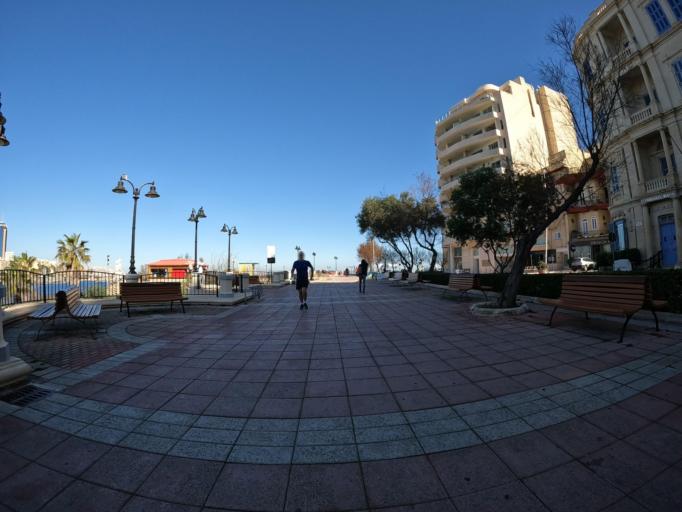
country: MT
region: Tas-Sliema
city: Sliema
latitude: 35.9171
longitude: 14.4985
